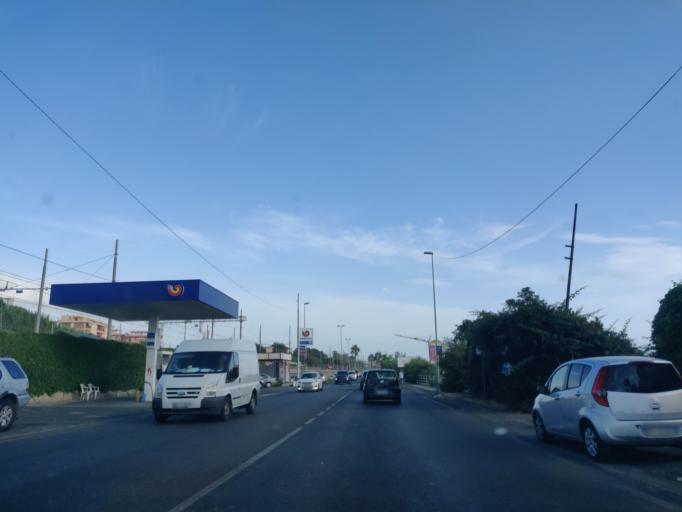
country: IT
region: Latium
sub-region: Citta metropolitana di Roma Capitale
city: Civitavecchia
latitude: 42.0822
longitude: 11.8064
